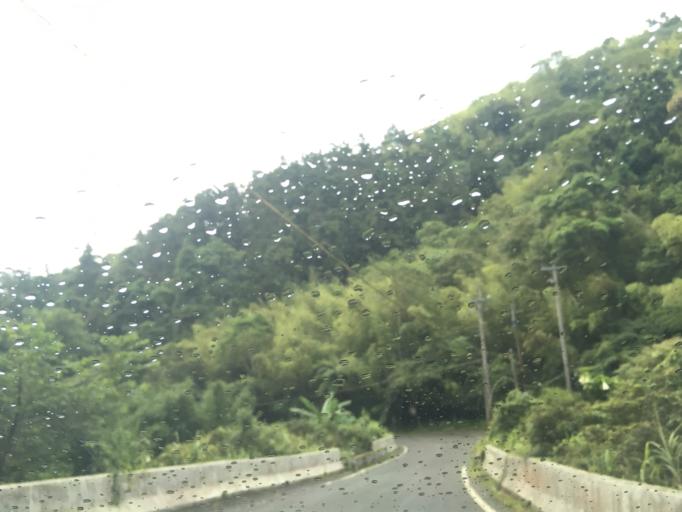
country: TW
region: Taiwan
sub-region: Yunlin
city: Douliu
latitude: 23.5603
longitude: 120.6095
